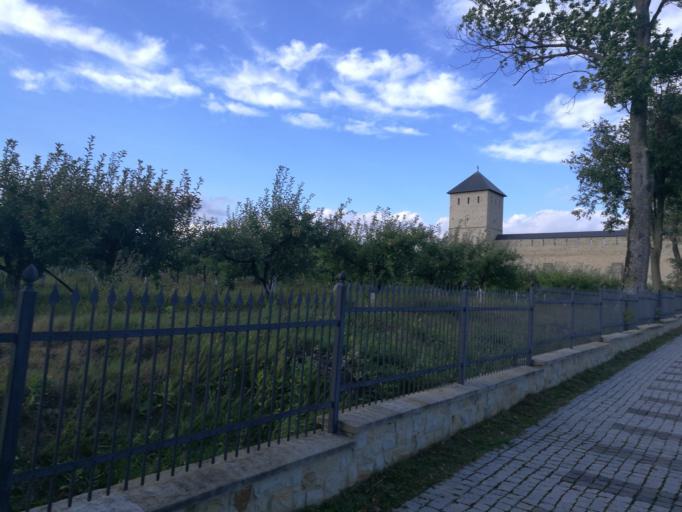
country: RO
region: Suceava
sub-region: Comuna Mitocu Dragomirnei
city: Mitocu Dragomirnei
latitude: 47.7569
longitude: 26.2286
